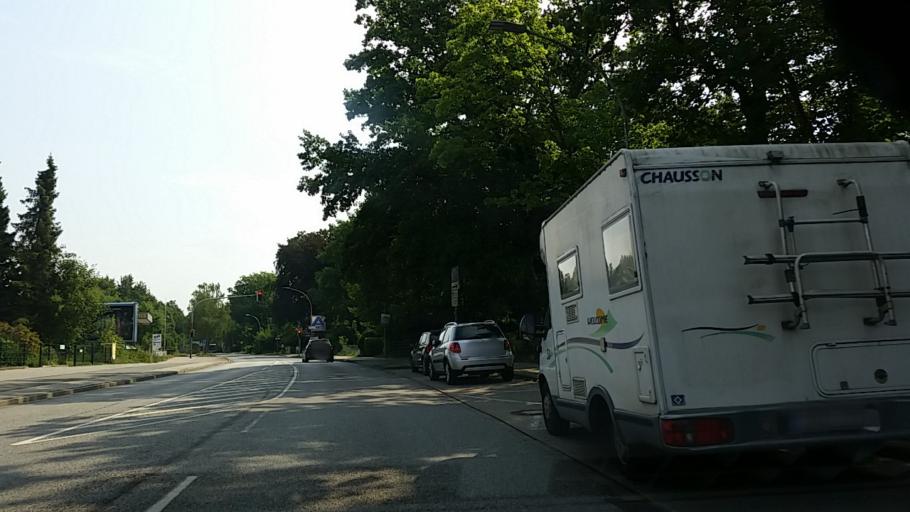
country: DE
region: Schleswig-Holstein
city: Glinde
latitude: 53.5428
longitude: 10.2151
